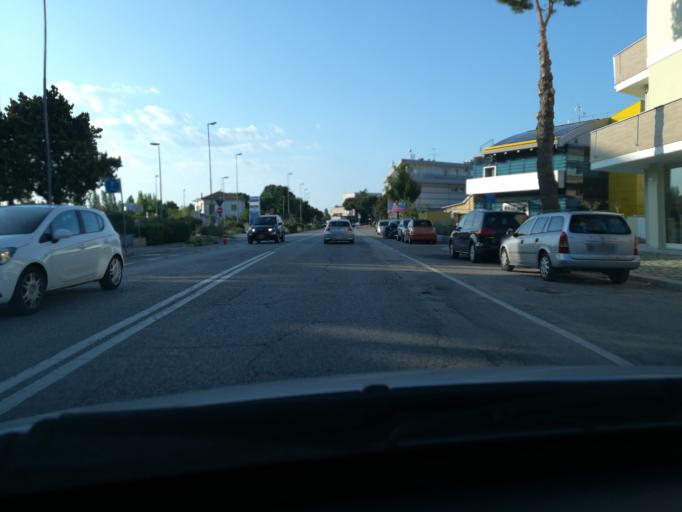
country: IT
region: Emilia-Romagna
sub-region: Provincia di Rimini
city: Riccione
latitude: 43.9959
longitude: 12.6485
